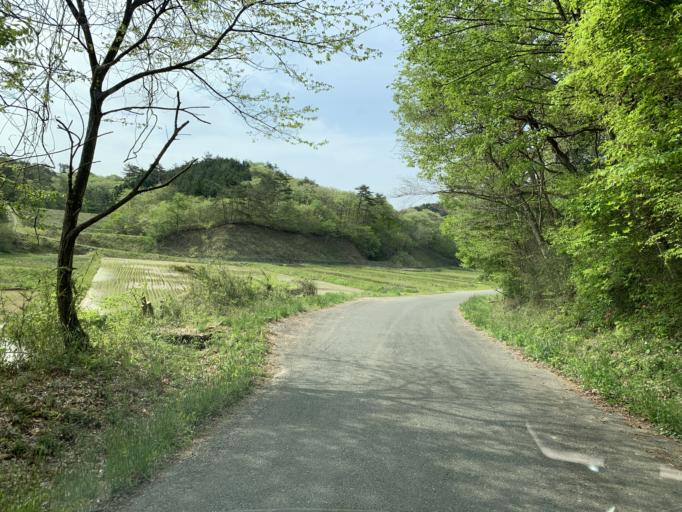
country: JP
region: Iwate
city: Ichinoseki
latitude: 38.8880
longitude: 141.0591
